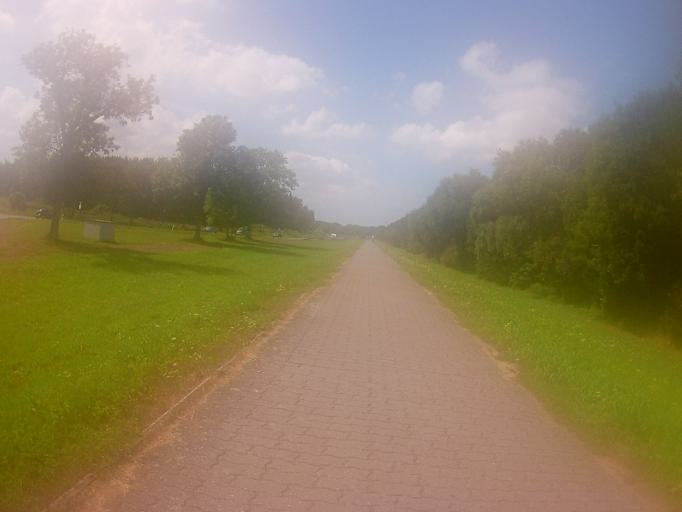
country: DE
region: Mecklenburg-Vorpommern
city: Koserow
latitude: 54.0640
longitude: 13.9809
